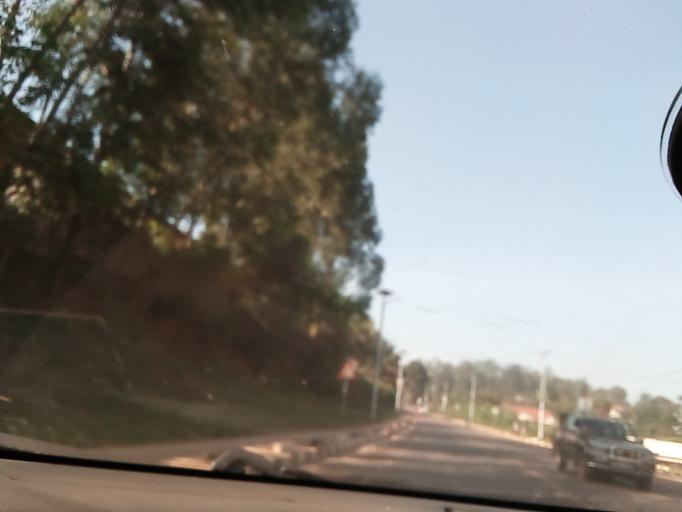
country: UG
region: Central Region
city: Masaka
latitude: -0.3248
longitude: 31.7380
